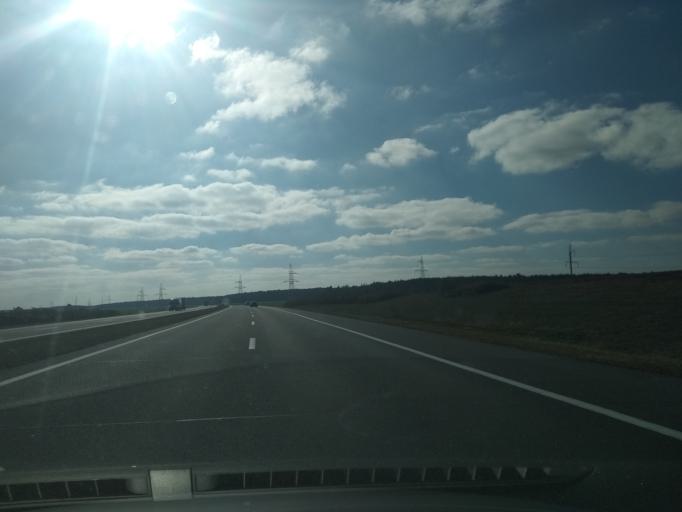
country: BY
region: Brest
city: Baranovichi
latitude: 53.1078
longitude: 25.8899
